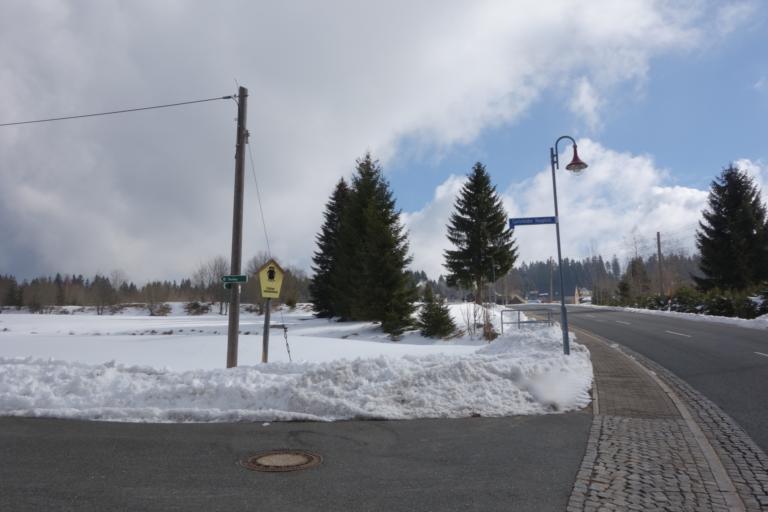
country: DE
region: Saxony
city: Eibenstock
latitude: 50.4333
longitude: 12.5983
